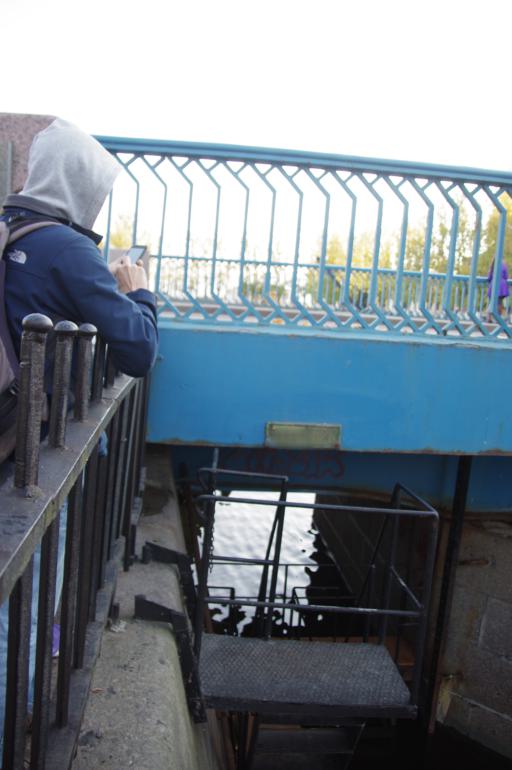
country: RU
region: St.-Petersburg
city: Kronshtadt
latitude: 59.9892
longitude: 29.7624
